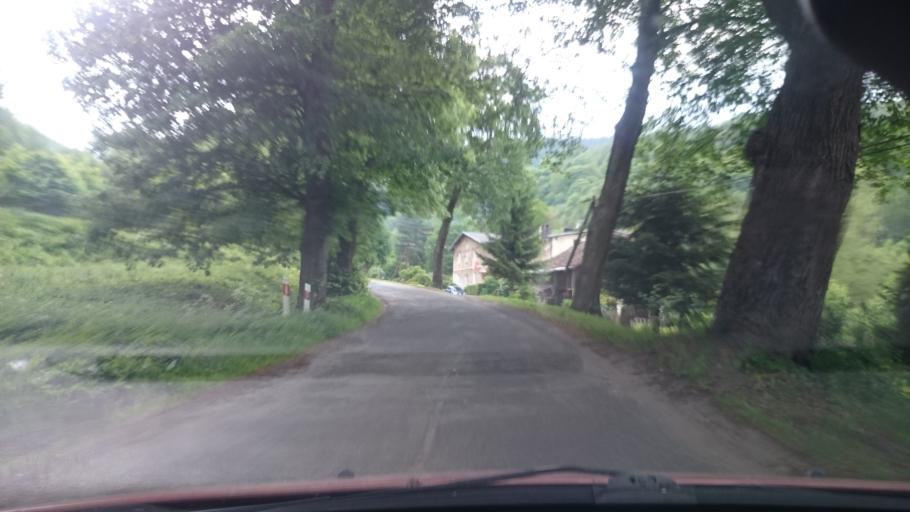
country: PL
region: Lower Silesian Voivodeship
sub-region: Powiat klodzki
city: Bystrzyca Klodzka
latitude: 50.3027
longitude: 16.5615
